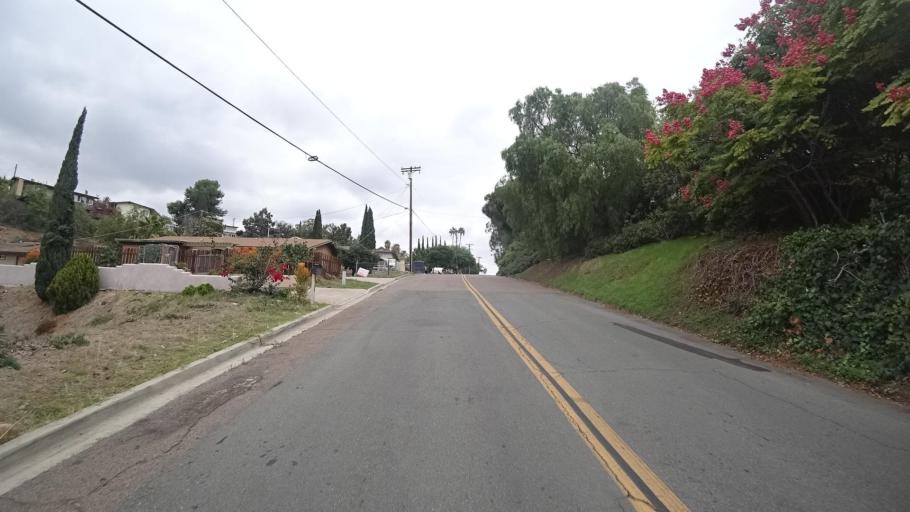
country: US
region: California
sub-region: San Diego County
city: Spring Valley
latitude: 32.7474
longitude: -117.0105
